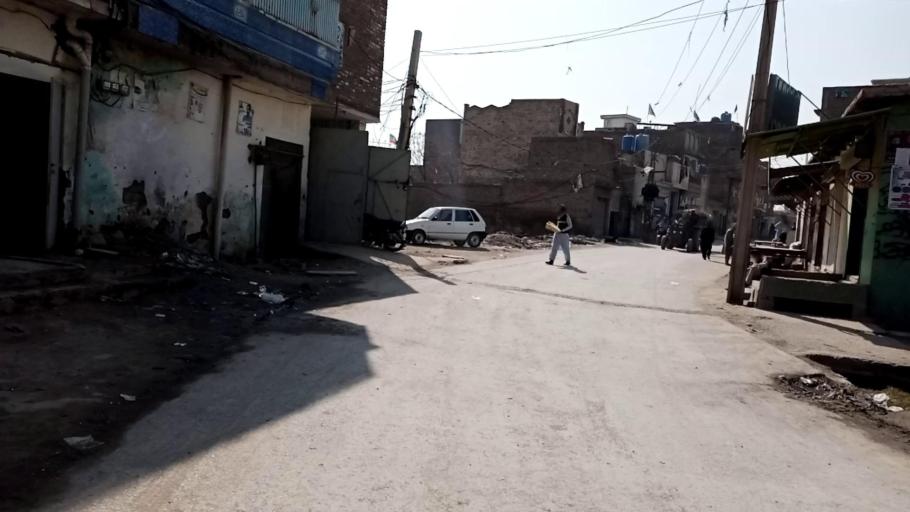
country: PK
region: Khyber Pakhtunkhwa
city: Peshawar
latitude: 34.0121
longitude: 71.5117
